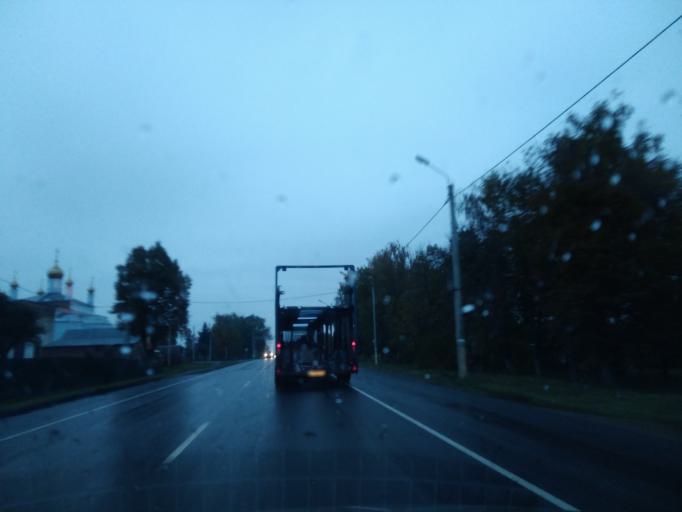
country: RU
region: Tula
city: Teploye
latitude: 53.6278
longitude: 37.5846
